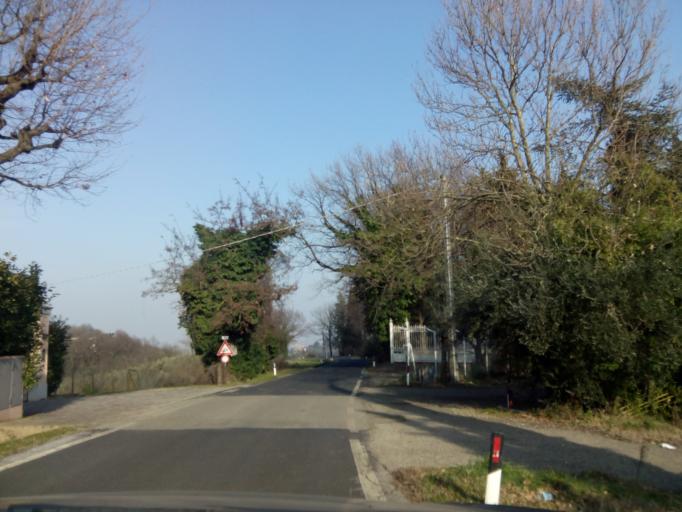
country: IT
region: Emilia-Romagna
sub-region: Provincia di Bologna
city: Imola
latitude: 44.3264
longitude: 11.6960
